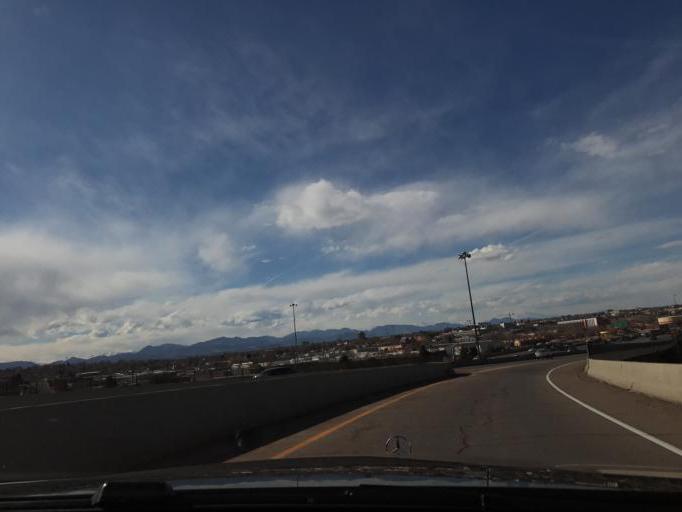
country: US
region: Colorado
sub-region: Denver County
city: Denver
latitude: 39.7270
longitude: -105.0128
